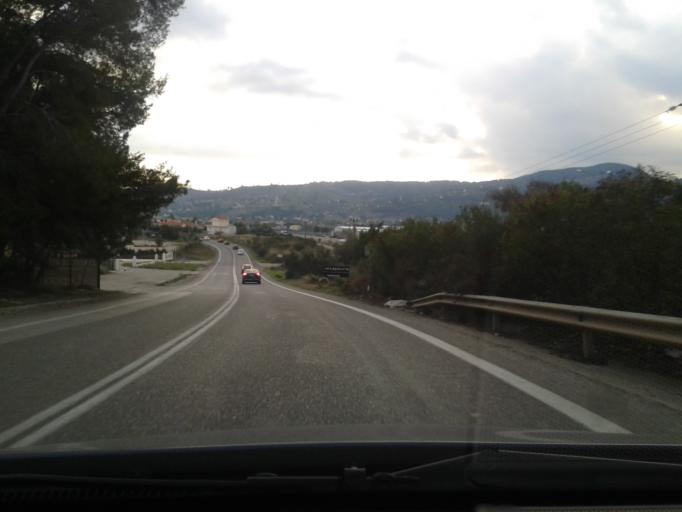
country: GR
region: Attica
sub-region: Nomarchia Anatolikis Attikis
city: Afidnes
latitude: 38.1985
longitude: 23.8533
